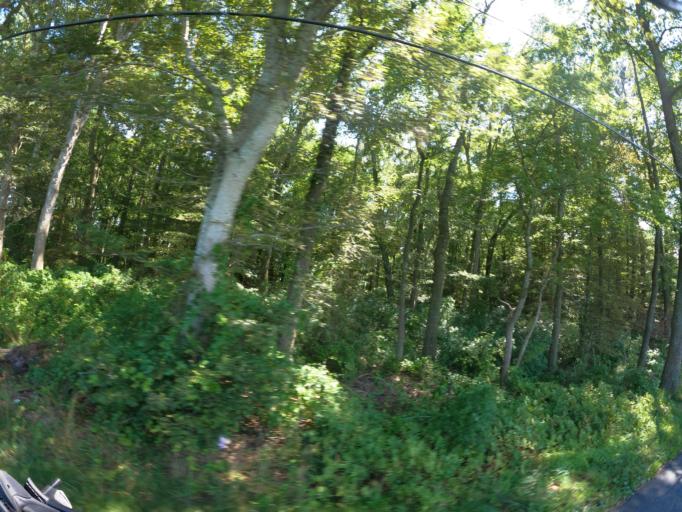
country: US
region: Delaware
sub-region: Sussex County
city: Selbyville
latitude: 38.4512
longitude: -75.1819
